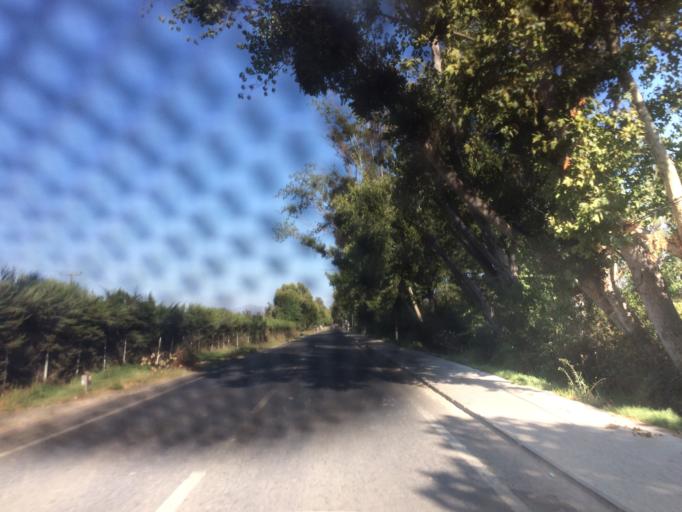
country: CL
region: Santiago Metropolitan
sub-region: Provincia de Melipilla
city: Melipilla
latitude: -33.4912
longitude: -71.1711
